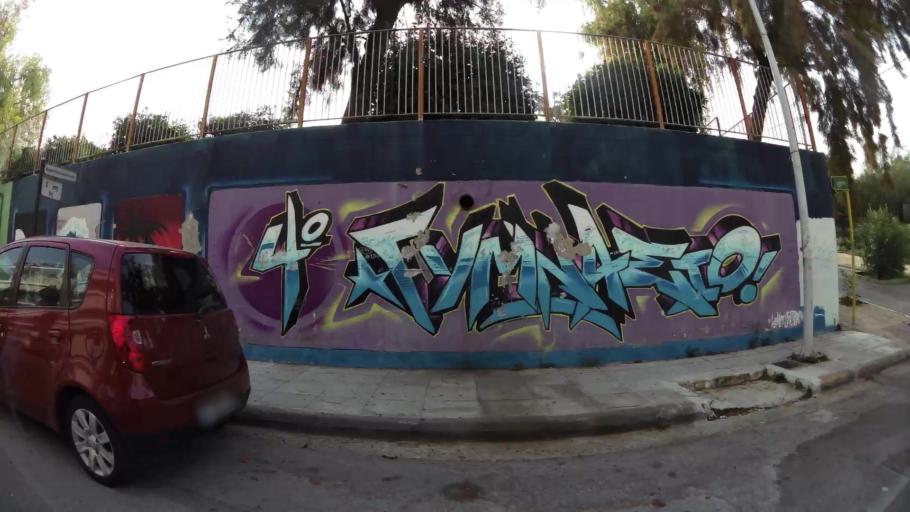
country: GR
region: Attica
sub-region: Nomarchia Athinas
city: Agios Dimitrios
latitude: 37.9281
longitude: 23.7219
